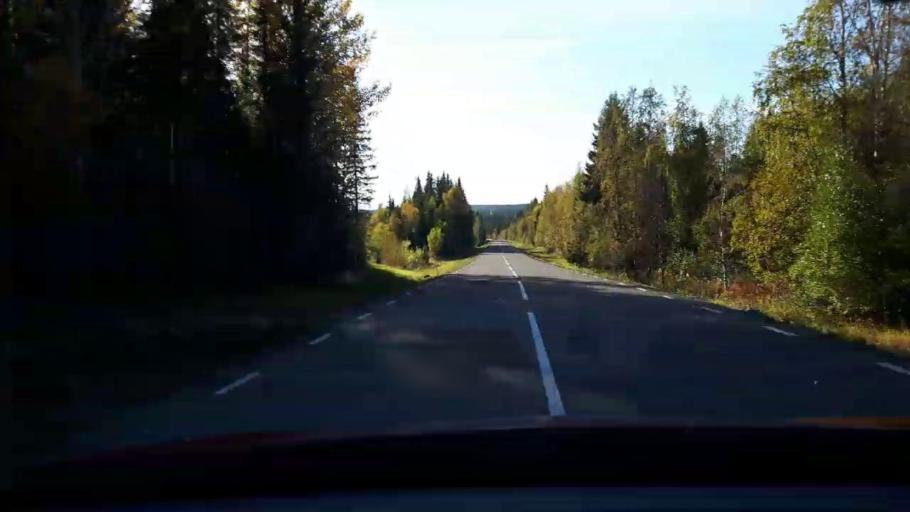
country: SE
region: Jaemtland
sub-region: Stroemsunds Kommun
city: Stroemsund
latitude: 63.8672
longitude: 15.1171
